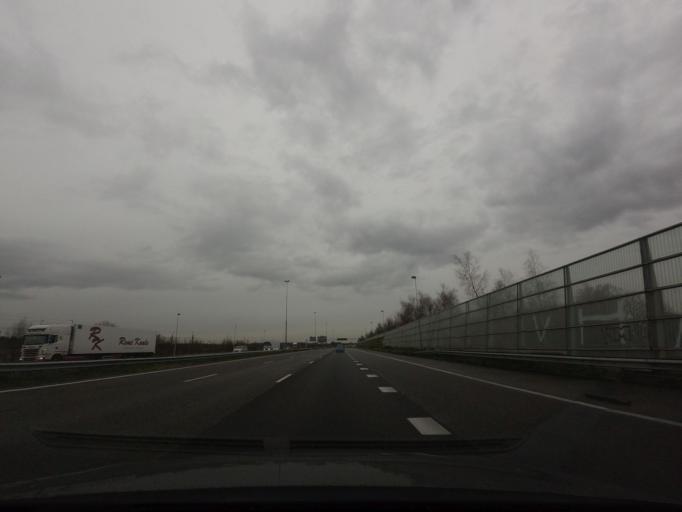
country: NL
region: North Brabant
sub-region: Gemeente Breda
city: Breda
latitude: 51.5592
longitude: 4.7354
